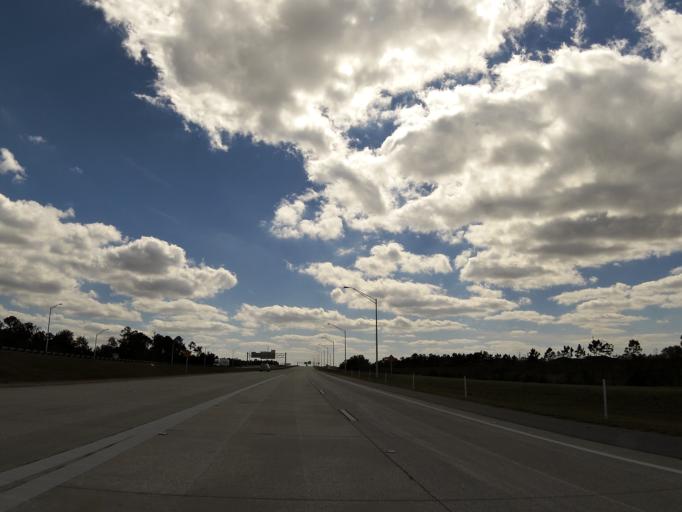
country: US
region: Florida
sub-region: Saint Johns County
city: Fruit Cove
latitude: 30.1095
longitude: -81.5153
